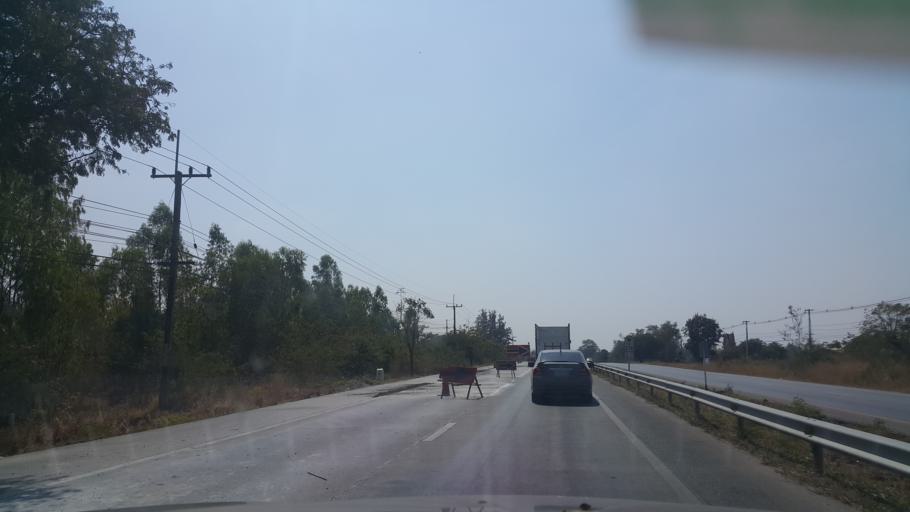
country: TH
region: Khon Kaen
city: Non Sila
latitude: 15.9294
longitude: 102.6698
